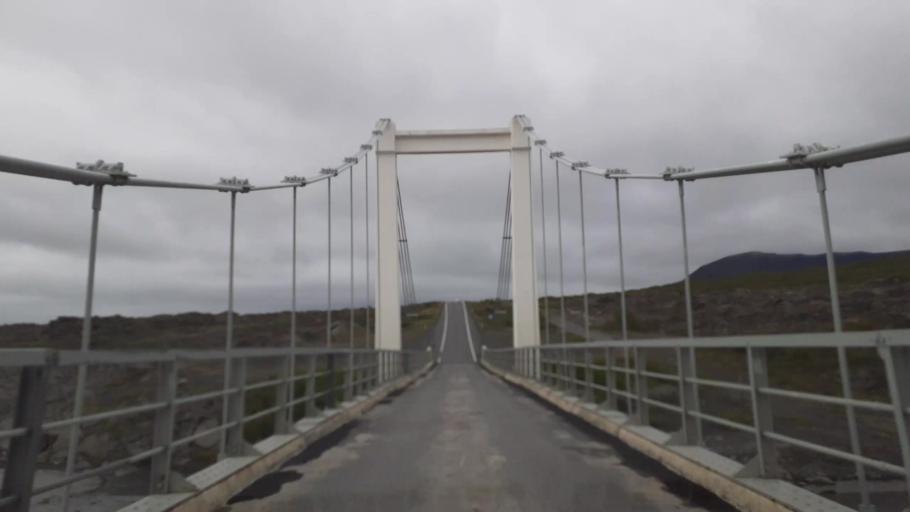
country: IS
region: Northeast
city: Husavik
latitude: 66.0329
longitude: -16.4437
